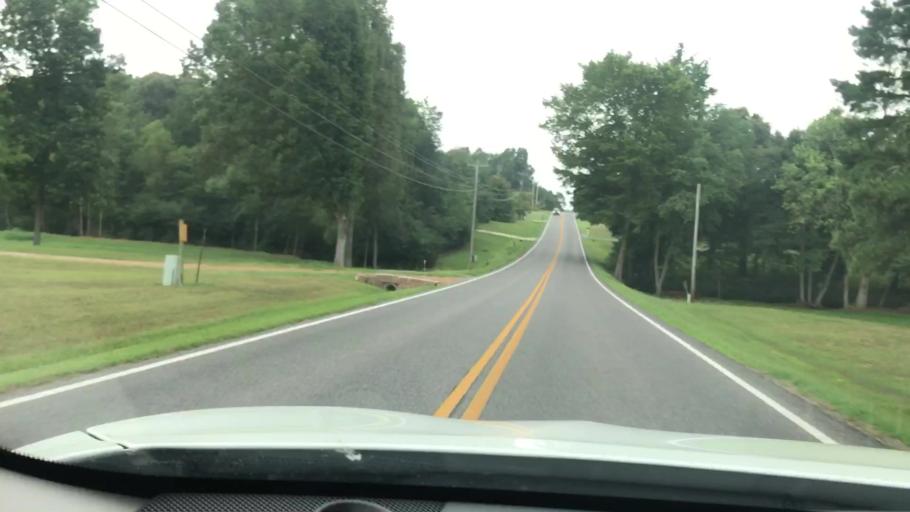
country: US
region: Kentucky
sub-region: Calloway County
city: Murray
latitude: 36.6812
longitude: -88.3003
